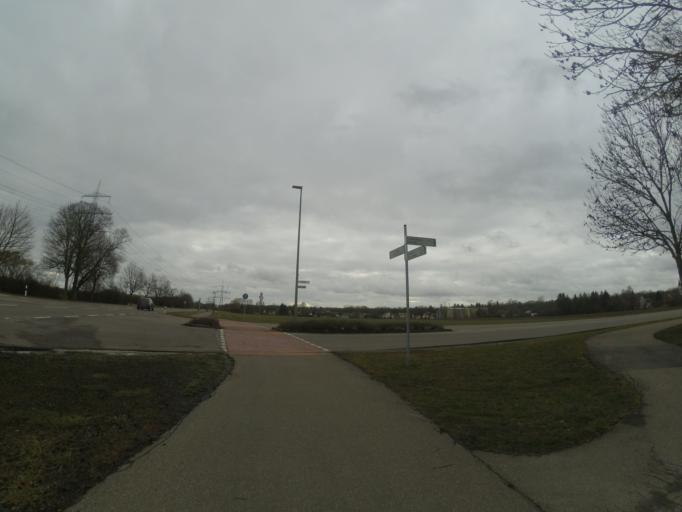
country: DE
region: Bavaria
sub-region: Swabia
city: Senden
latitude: 48.2991
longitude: 10.0584
